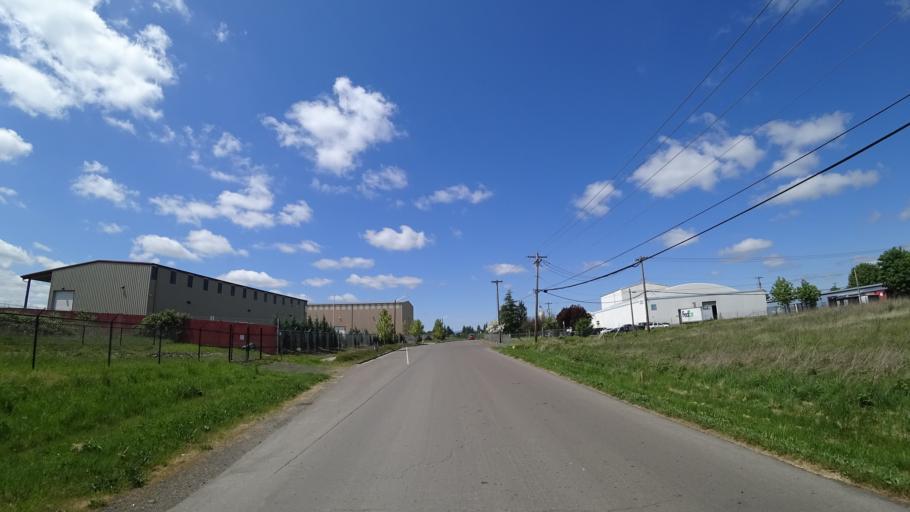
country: US
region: Oregon
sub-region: Washington County
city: Hillsboro
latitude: 45.5127
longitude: -122.9952
